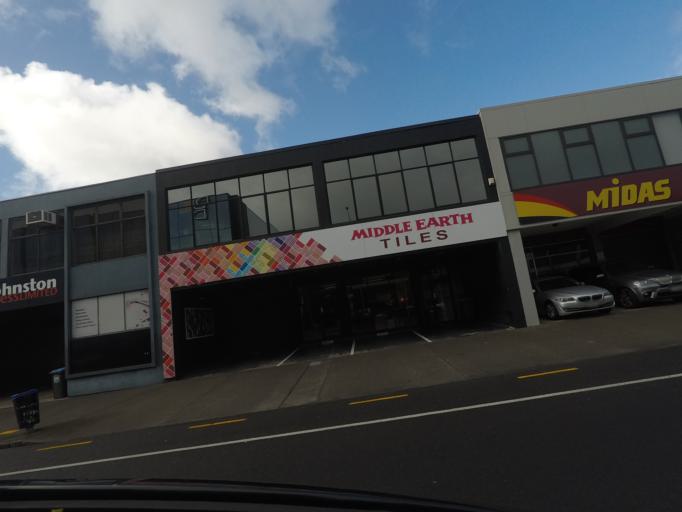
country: NZ
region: Auckland
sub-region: Auckland
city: Auckland
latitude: -36.8622
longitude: 174.7495
